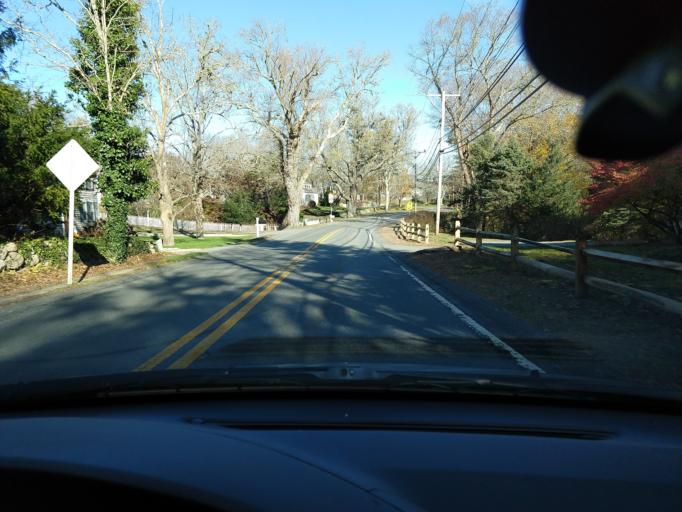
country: US
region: Massachusetts
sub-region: Barnstable County
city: Barnstable
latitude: 41.6996
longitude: -70.3289
